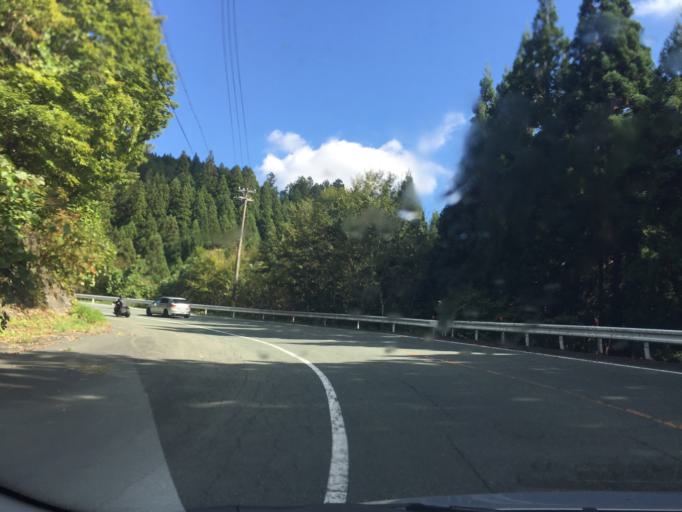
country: JP
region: Nagano
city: Iida
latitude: 35.2231
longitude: 137.6955
